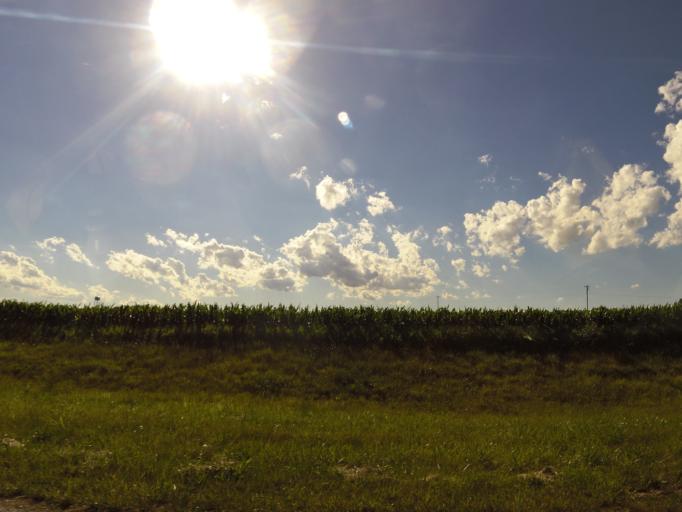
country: US
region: Missouri
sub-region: Marion County
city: Hannibal
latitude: 39.7025
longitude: -91.4201
